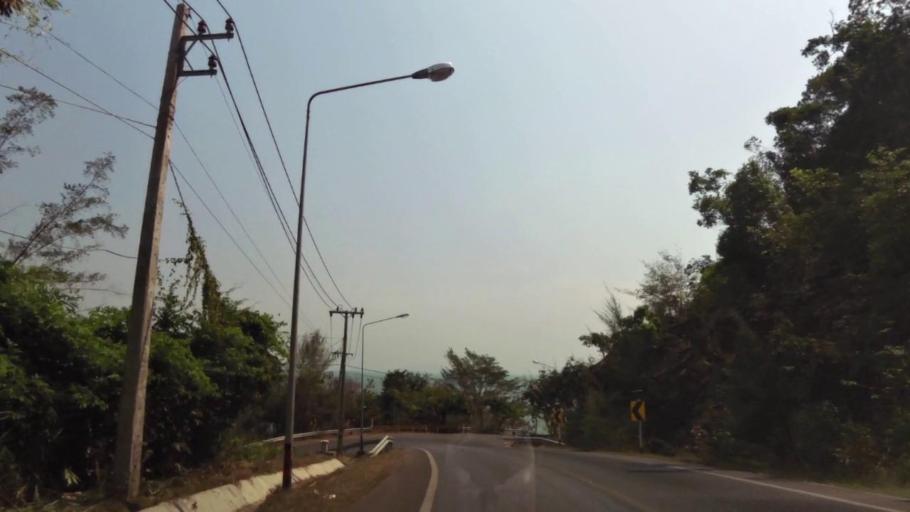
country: TH
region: Chanthaburi
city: Tha Mai
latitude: 12.5244
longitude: 101.9481
